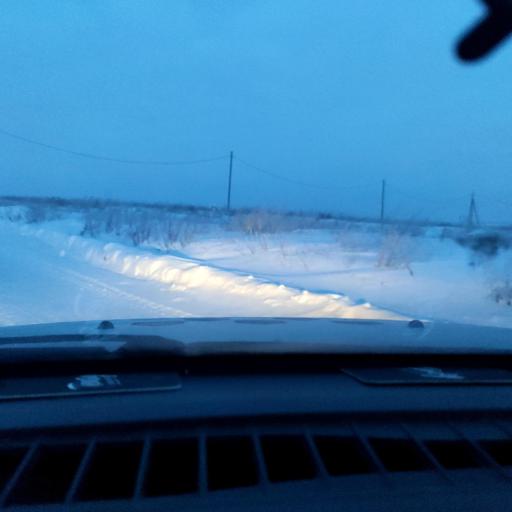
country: RU
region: Perm
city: Kultayevo
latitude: 57.8752
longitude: 55.9693
